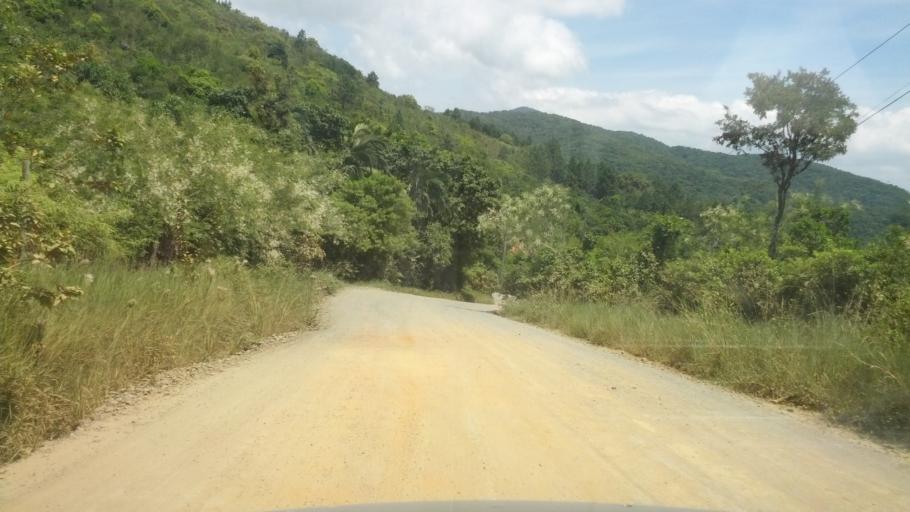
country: BR
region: Santa Catarina
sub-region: Porto Belo
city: Porto Belo
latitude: -27.1596
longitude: -48.5325
